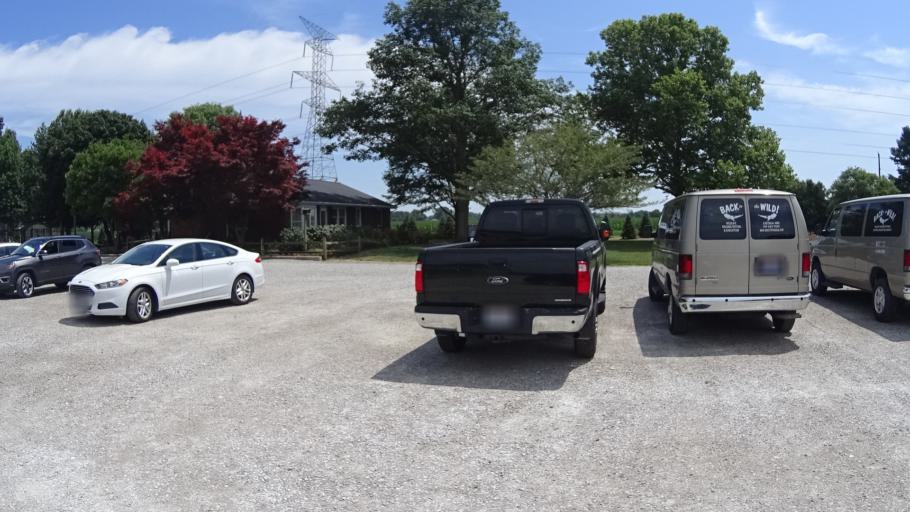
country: US
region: Ohio
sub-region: Erie County
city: Sandusky
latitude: 41.3867
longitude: -82.7683
